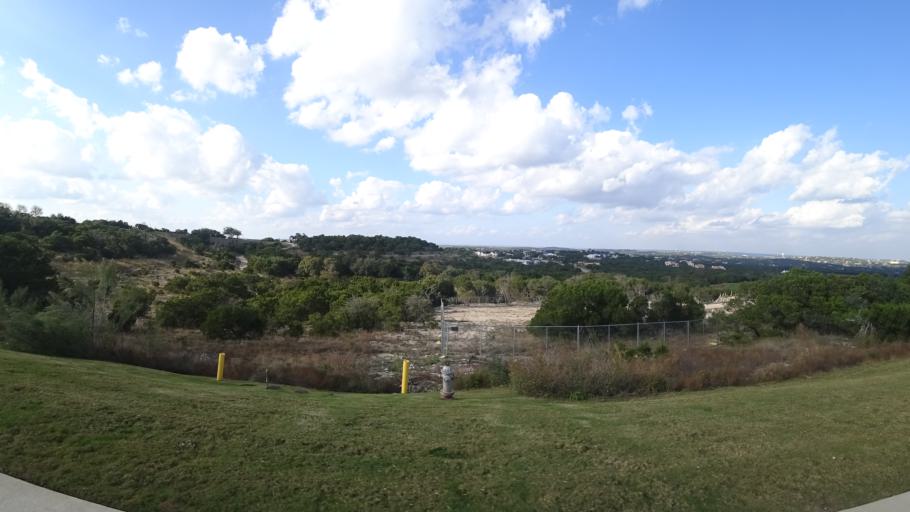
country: US
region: Texas
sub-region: Travis County
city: Barton Creek
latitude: 30.2627
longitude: -97.8797
